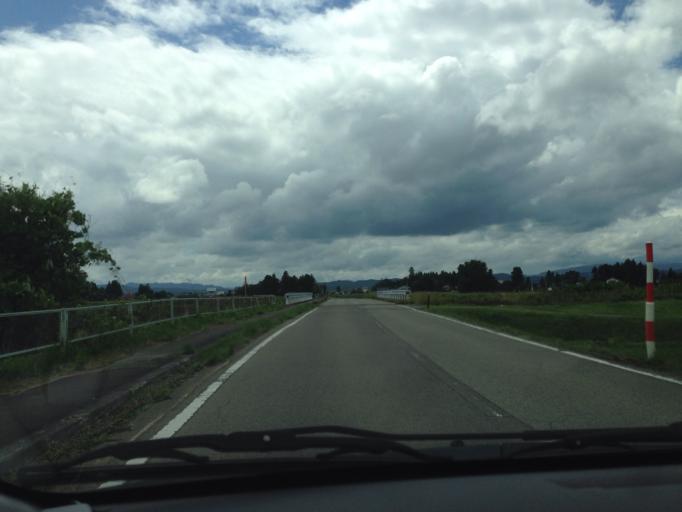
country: JP
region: Fukushima
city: Kitakata
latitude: 37.6115
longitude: 139.9024
